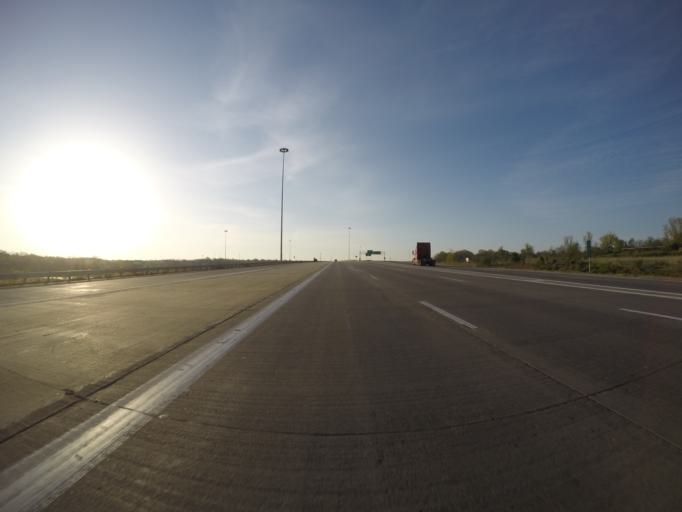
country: US
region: Missouri
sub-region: Jackson County
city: Grandview
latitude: 38.9354
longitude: -94.5330
